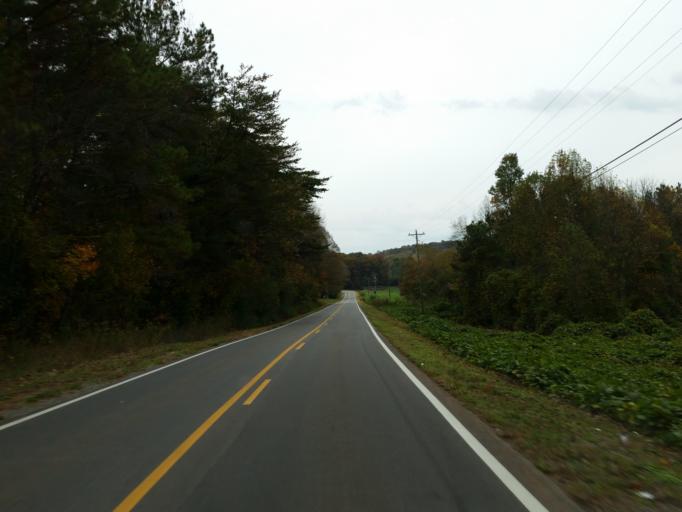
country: US
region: Georgia
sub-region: Gilmer County
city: Ellijay
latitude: 34.6590
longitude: -84.3616
